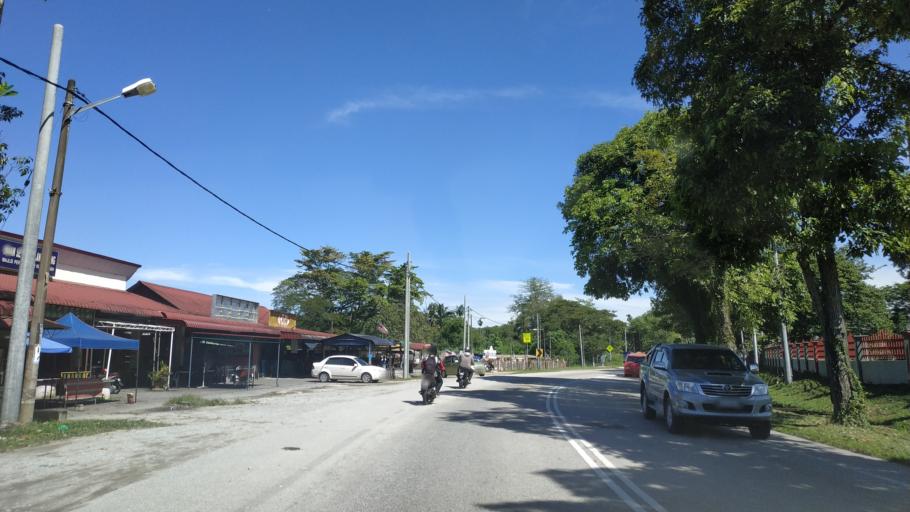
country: MY
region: Kedah
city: Kulim
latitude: 5.3508
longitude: 100.5364
